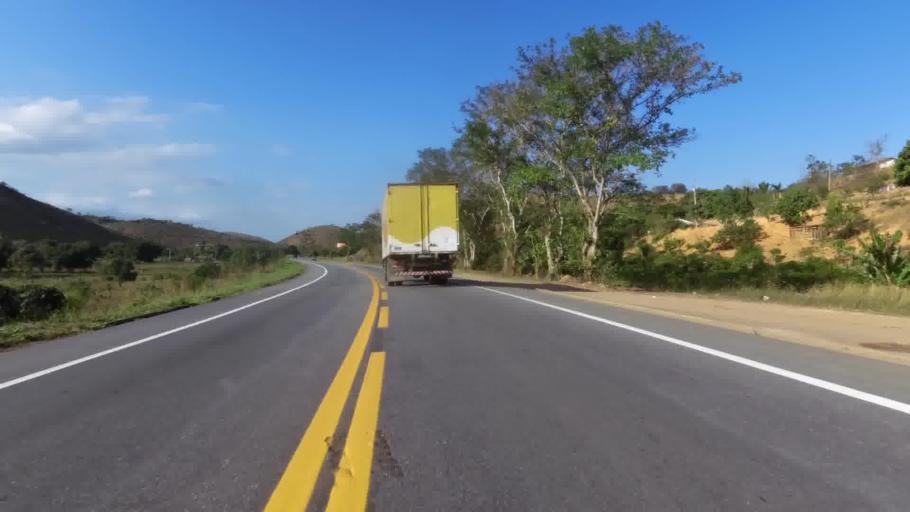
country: BR
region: Espirito Santo
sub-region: Mimoso Do Sul
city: Mimoso do Sul
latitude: -21.1734
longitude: -41.2935
